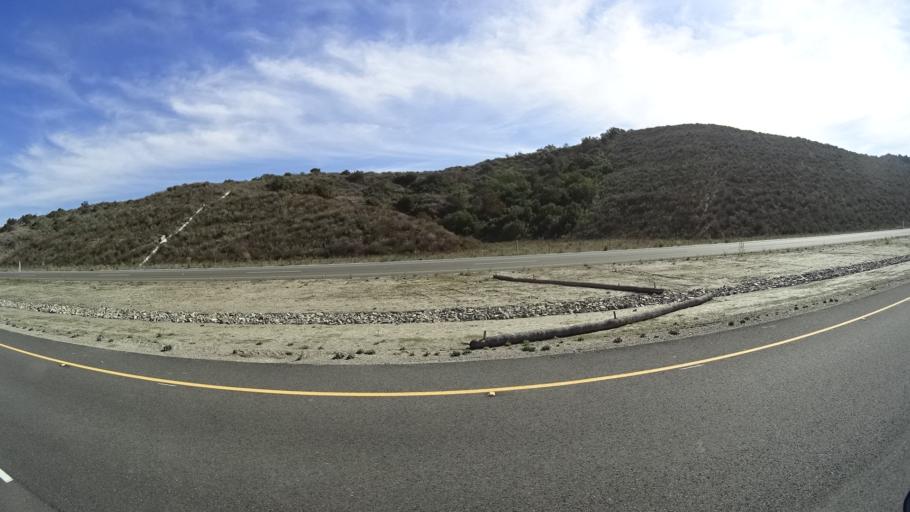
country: US
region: California
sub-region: Orange County
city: Ladera Ranch
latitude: 33.5350
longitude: -117.5956
